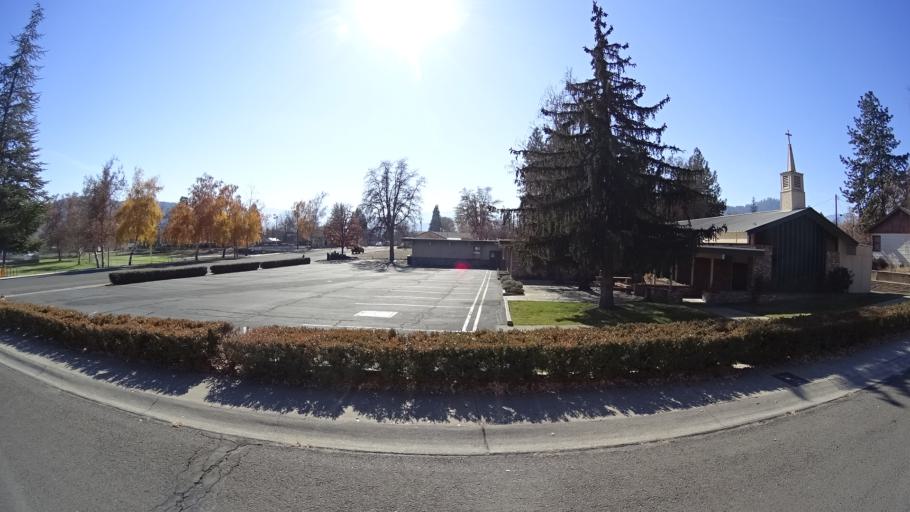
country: US
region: California
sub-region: Siskiyou County
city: Yreka
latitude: 41.7395
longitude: -122.6412
